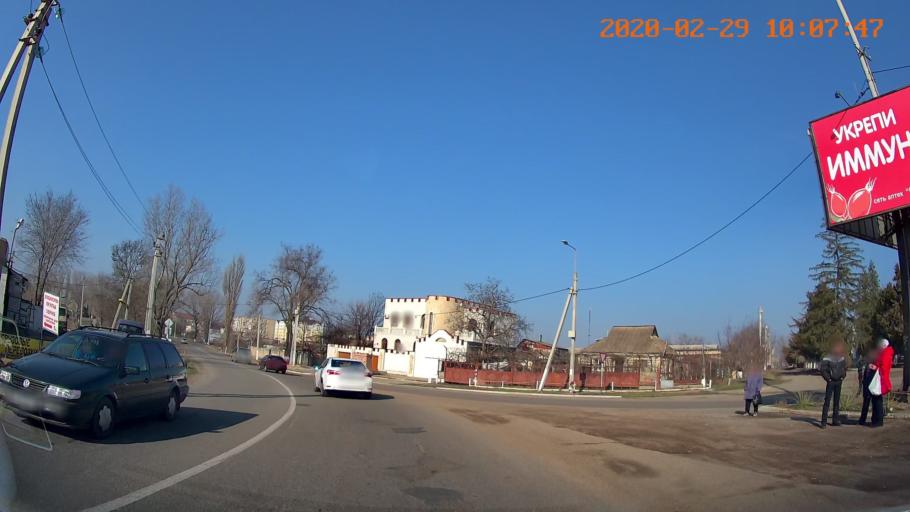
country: MD
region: Telenesti
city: Tiraspolul Nou
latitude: 46.8230
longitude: 29.6634
